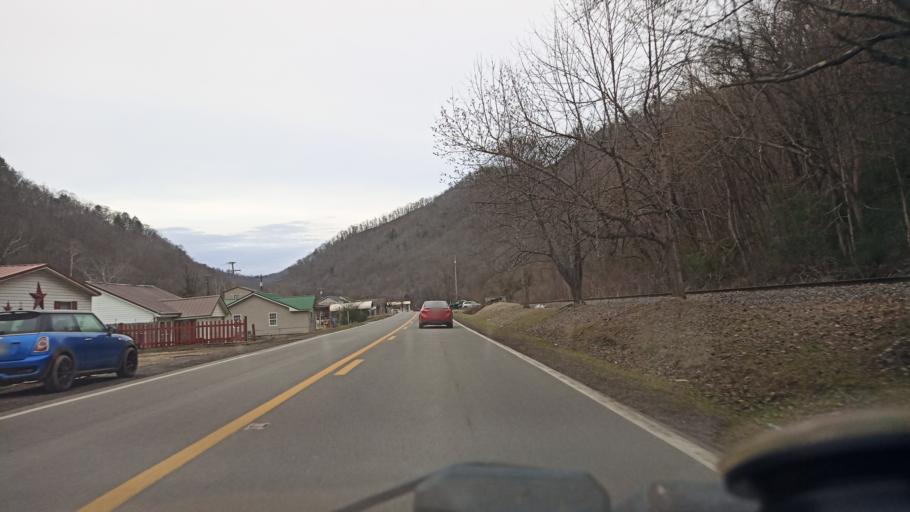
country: US
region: West Virginia
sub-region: Logan County
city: Mallory
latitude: 37.7115
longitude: -81.8674
